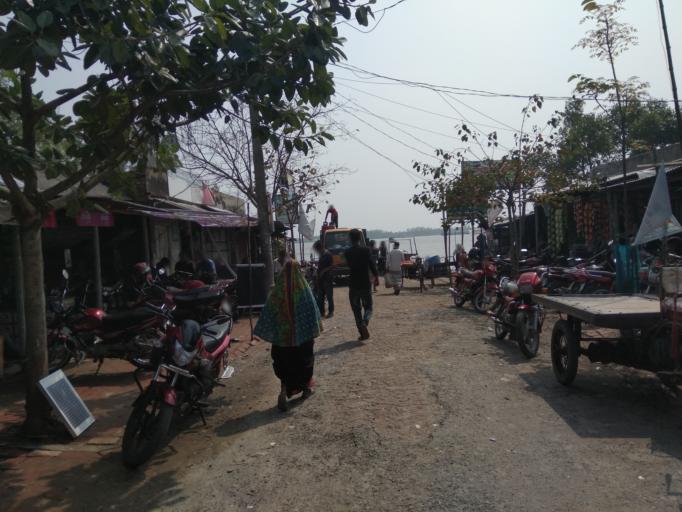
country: IN
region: West Bengal
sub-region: North 24 Parganas
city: Gosaba
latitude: 22.2503
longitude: 89.2420
